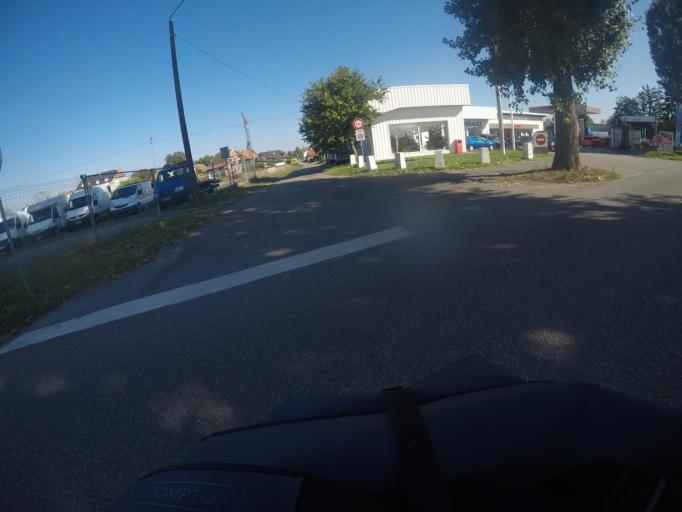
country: FR
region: Alsace
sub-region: Departement du Haut-Rhin
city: Ottmarsheim
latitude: 47.7837
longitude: 7.5056
